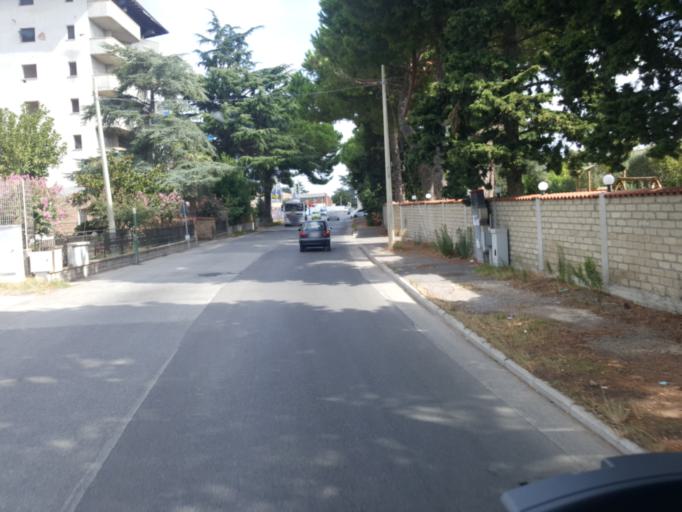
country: IT
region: Latium
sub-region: Citta metropolitana di Roma Capitale
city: Area Produttiva
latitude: 41.6847
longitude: 12.5116
